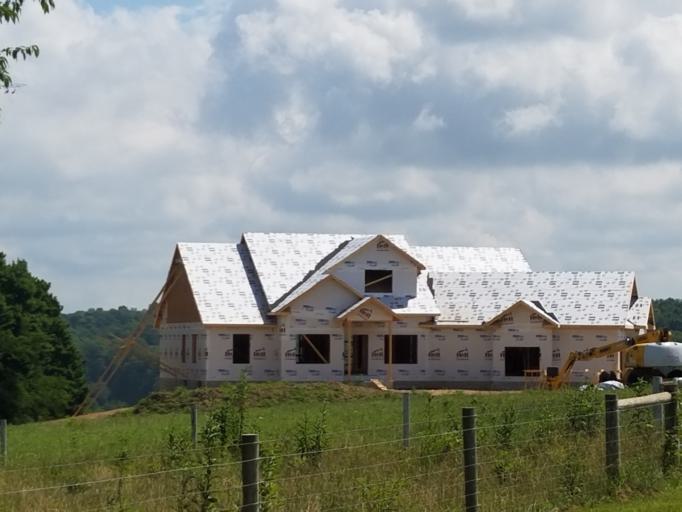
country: US
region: Ohio
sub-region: Knox County
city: Danville
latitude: 40.5067
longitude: -82.3719
